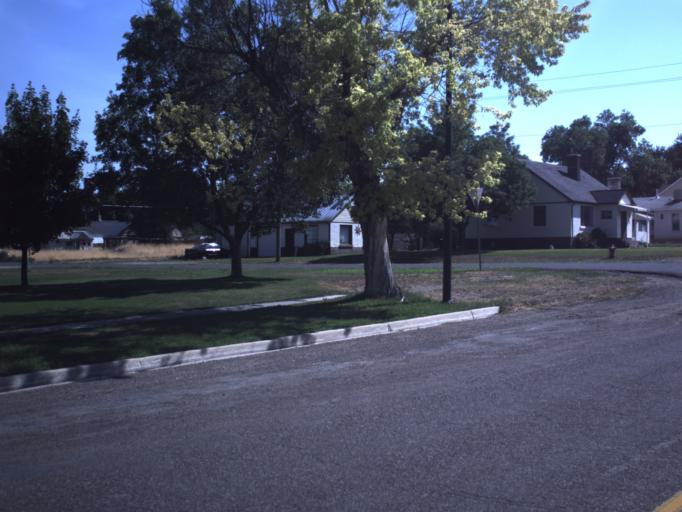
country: US
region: Utah
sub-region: Sanpete County
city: Mount Pleasant
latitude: 39.5467
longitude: -111.4538
